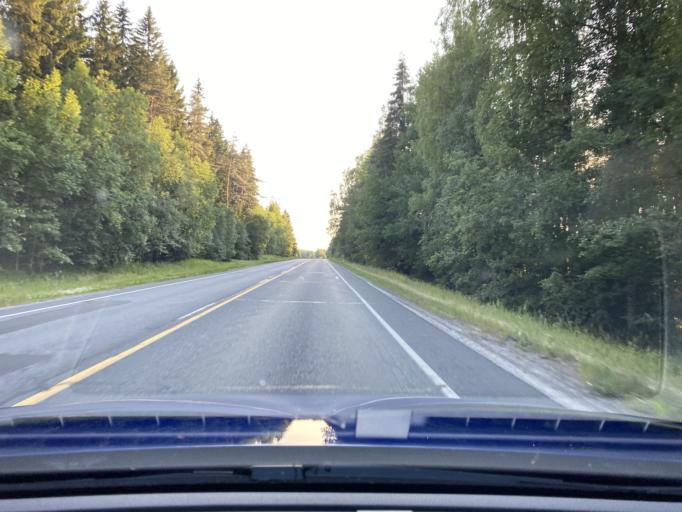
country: FI
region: Haeme
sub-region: Forssa
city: Tammela
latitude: 60.8267
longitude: 23.9374
